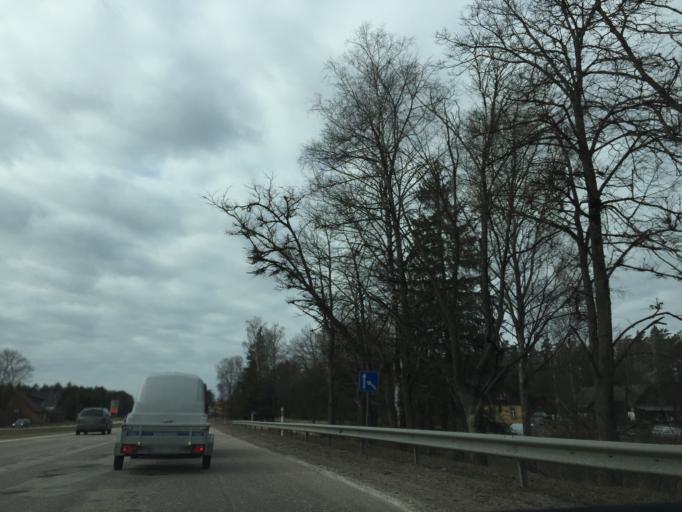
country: LV
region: Seja
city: Loja
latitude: 57.1158
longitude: 24.6345
